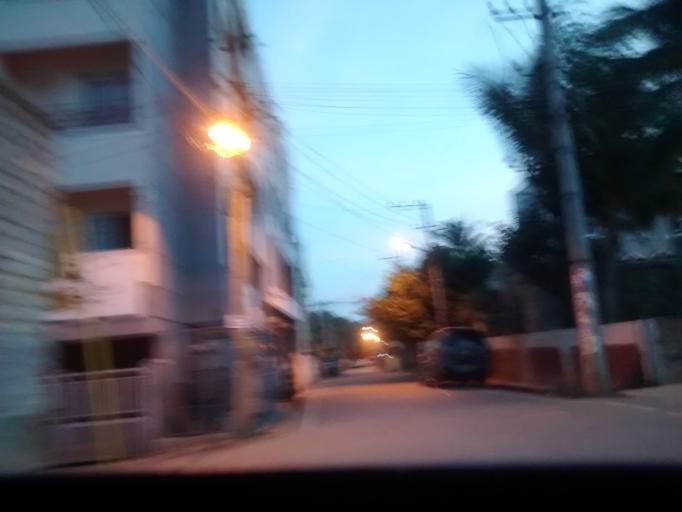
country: IN
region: Karnataka
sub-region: Bangalore Urban
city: Bangalore
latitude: 12.9681
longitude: 77.6680
